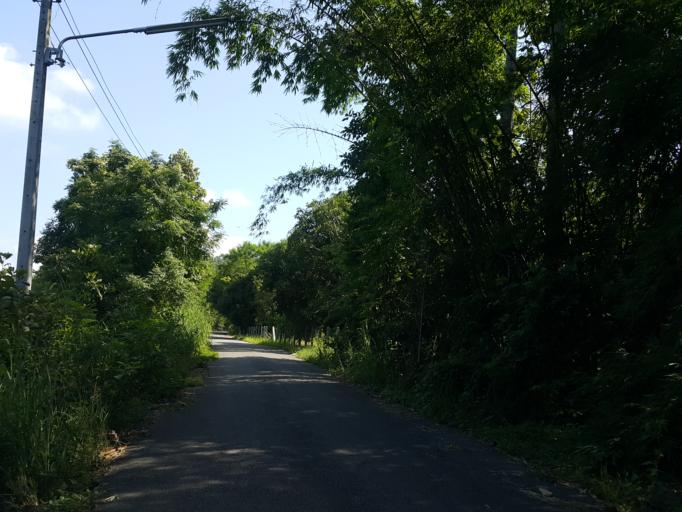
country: TH
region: Chiang Mai
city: Mae On
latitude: 18.8083
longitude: 99.1819
